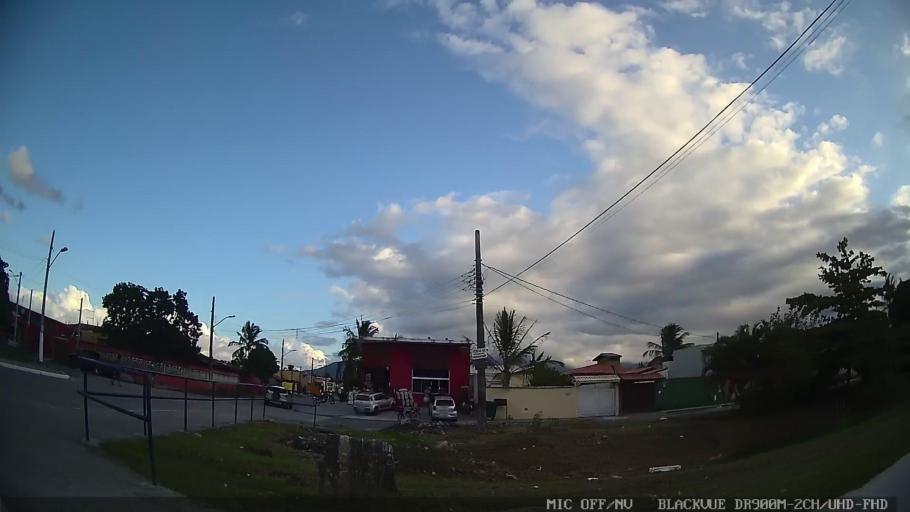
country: BR
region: Sao Paulo
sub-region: Caraguatatuba
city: Caraguatatuba
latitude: -23.6658
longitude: -45.4432
